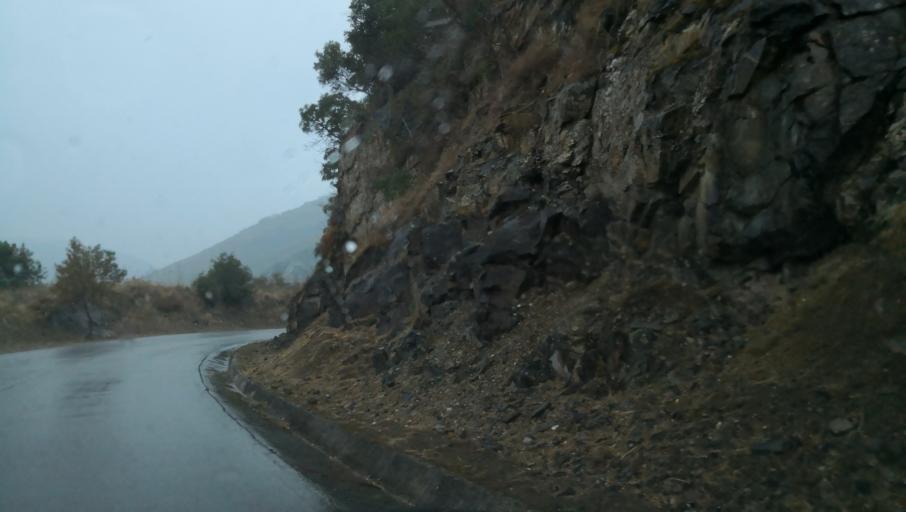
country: PT
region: Vila Real
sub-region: Peso da Regua
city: Peso da Regua
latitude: 41.1726
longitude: -7.7495
